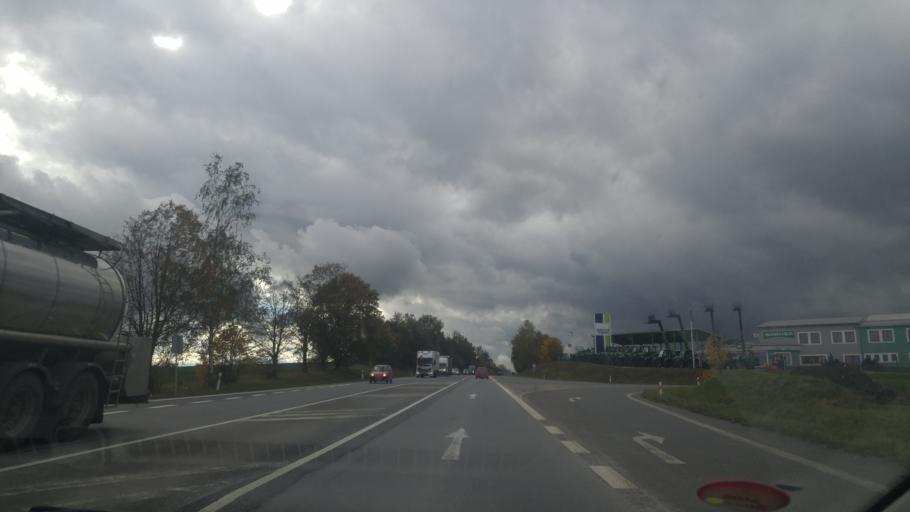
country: CZ
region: Jihocesky
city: Sevetin
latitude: 49.1261
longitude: 14.6033
